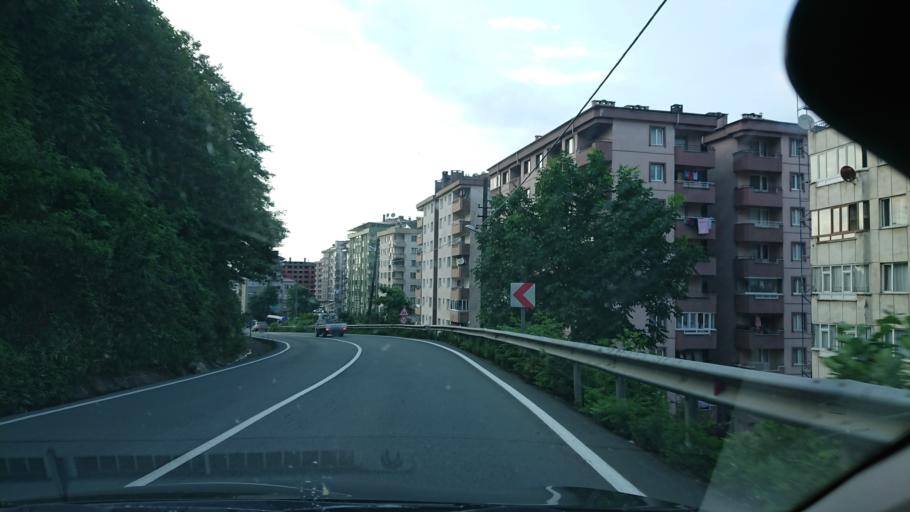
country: TR
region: Rize
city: Cayeli
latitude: 41.0791
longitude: 40.7133
